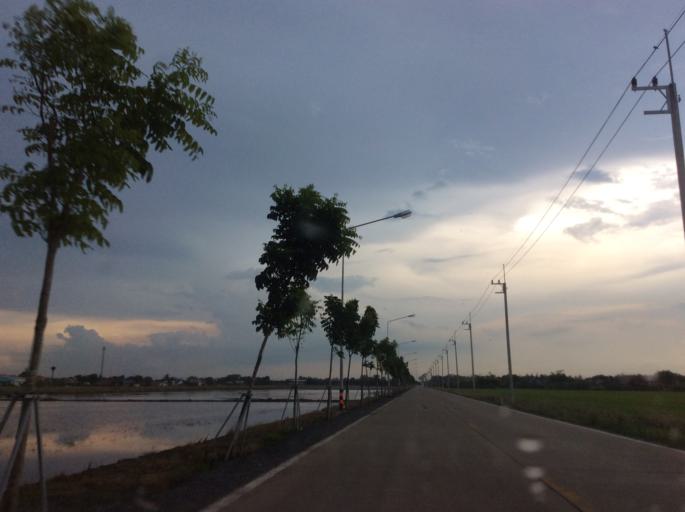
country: TH
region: Pathum Thani
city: Thanyaburi
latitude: 14.0029
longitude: 100.7389
